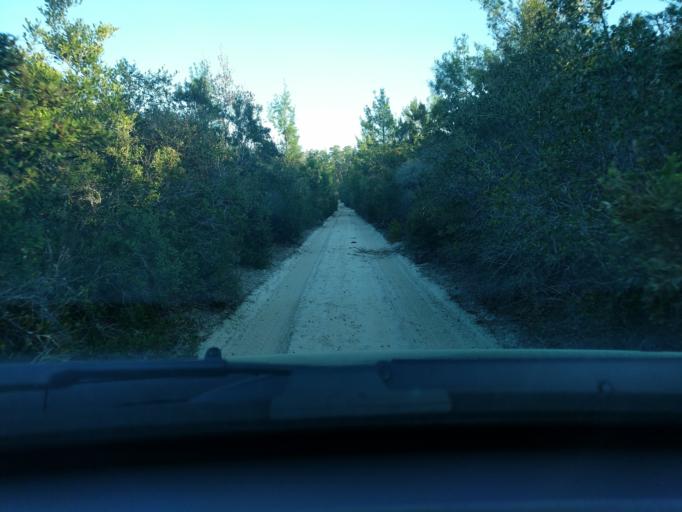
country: US
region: Florida
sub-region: Lake County
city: Astor
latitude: 29.2170
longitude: -81.7409
